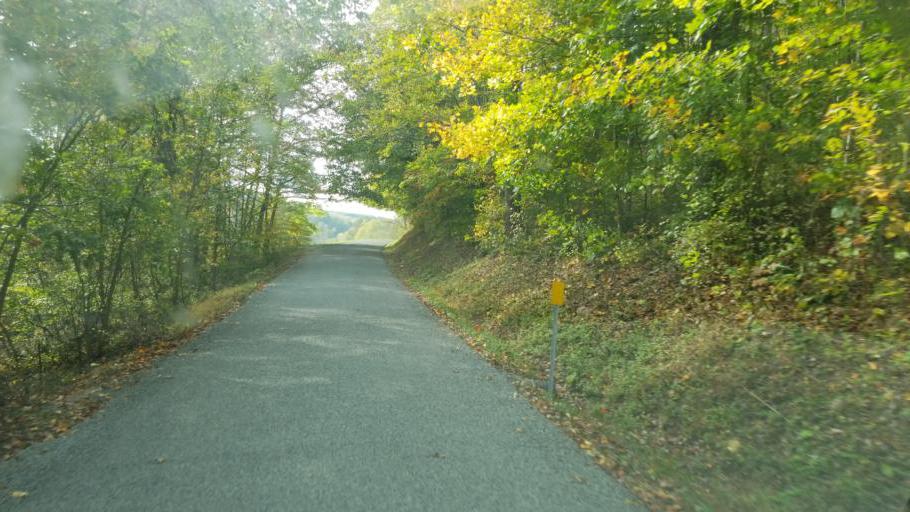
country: US
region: Ohio
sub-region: Holmes County
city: Millersburg
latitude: 40.5342
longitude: -81.8688
